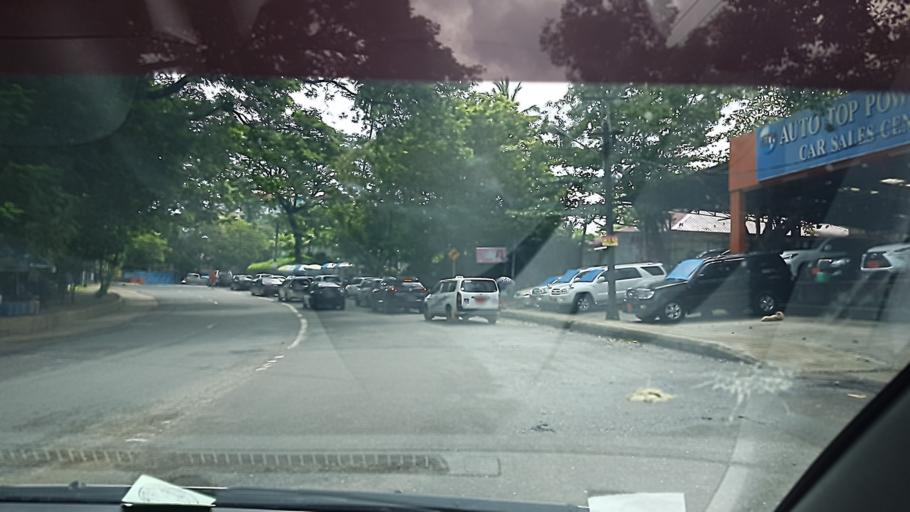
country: MM
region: Yangon
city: Yangon
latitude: 16.8072
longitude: 96.1520
